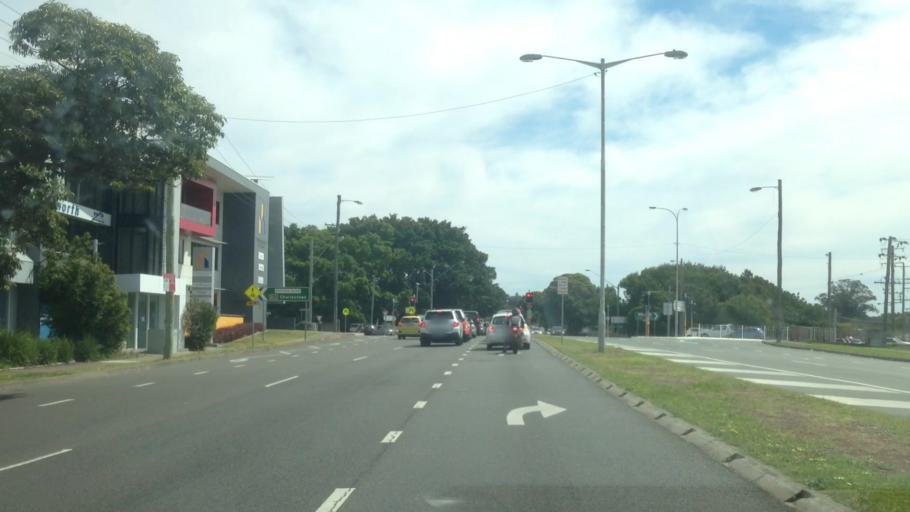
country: AU
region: New South Wales
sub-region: Newcastle
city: Broadmeadow
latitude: -32.9233
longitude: 151.7239
